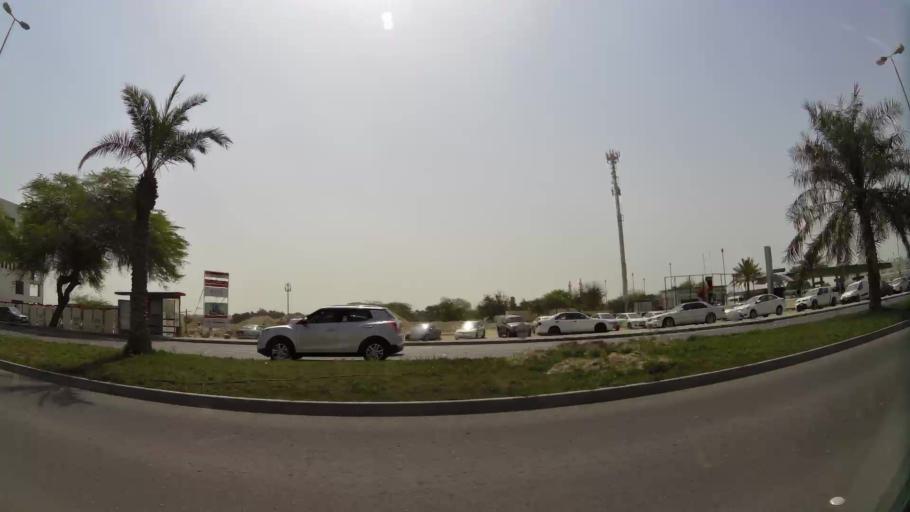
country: BH
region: Manama
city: Jidd Hafs
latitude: 26.2175
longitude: 50.4810
